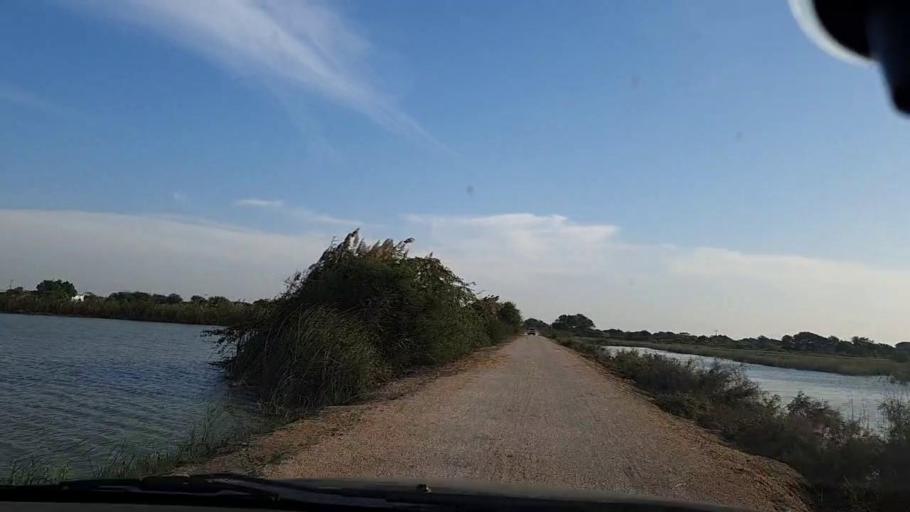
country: PK
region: Sindh
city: Mirpur Batoro
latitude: 24.6536
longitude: 68.2933
